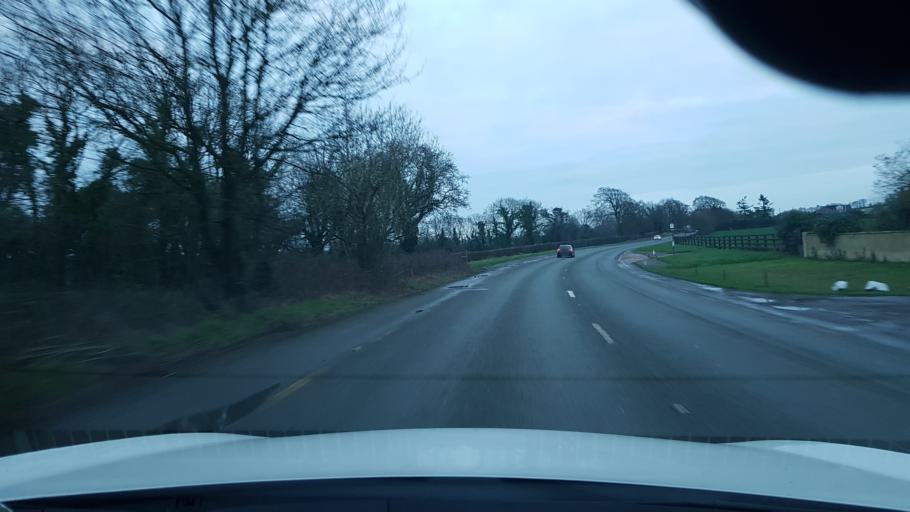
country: IE
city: Kentstown
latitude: 53.5895
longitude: -6.5969
